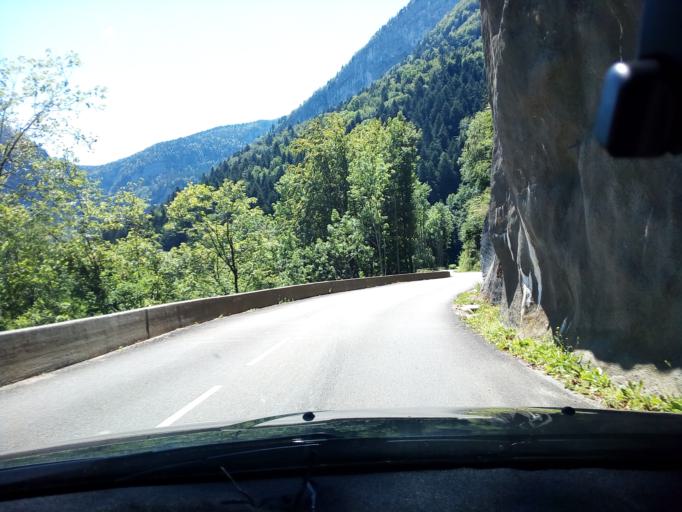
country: FR
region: Rhone-Alpes
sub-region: Departement de l'Isere
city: Meaudre
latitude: 45.0820
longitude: 5.4823
